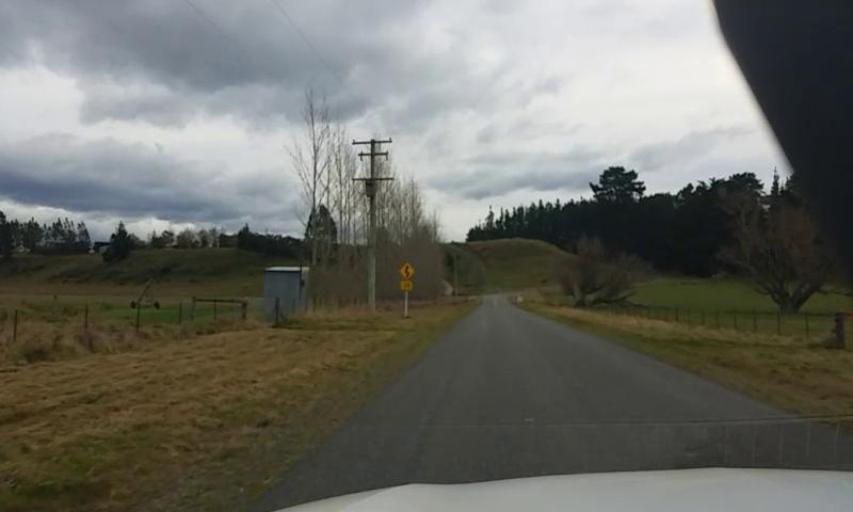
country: NZ
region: Canterbury
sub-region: Waimakariri District
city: Kaiapoi
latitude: -43.3002
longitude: 172.4378
